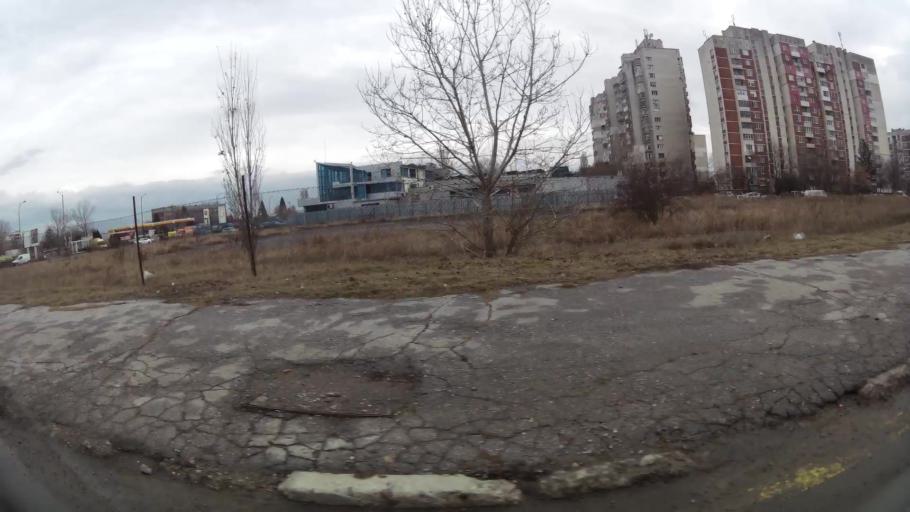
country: BG
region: Sofiya
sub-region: Obshtina Bozhurishte
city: Bozhurishte
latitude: 42.7328
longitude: 23.2500
